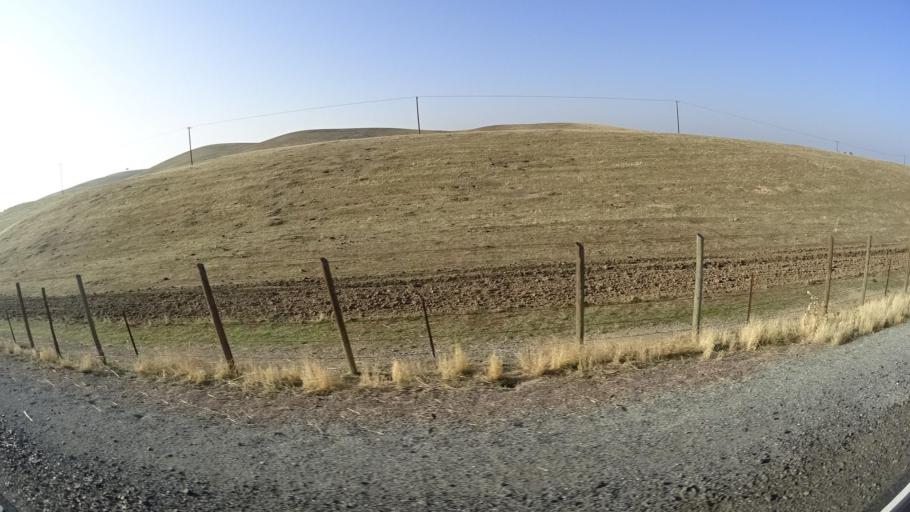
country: US
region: California
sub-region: Tulare County
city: Richgrove
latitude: 35.7578
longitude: -119.0237
